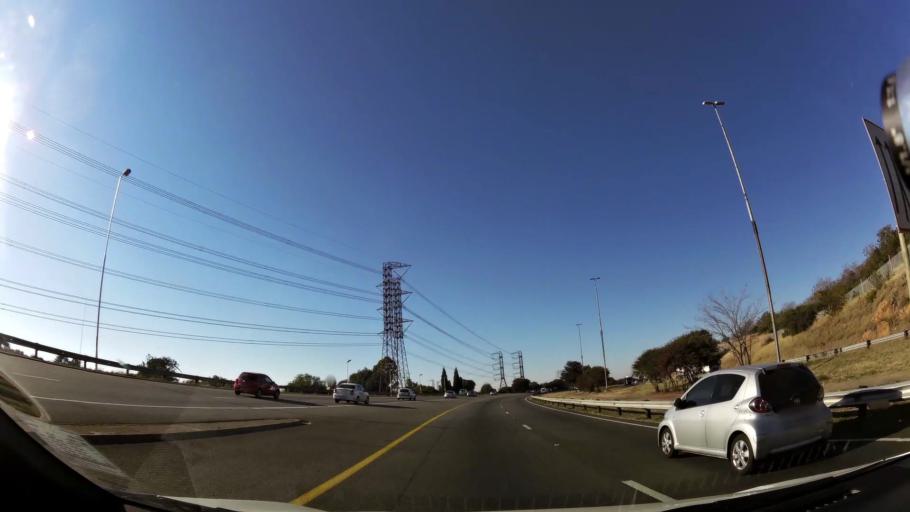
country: ZA
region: Gauteng
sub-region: Ekurhuleni Metropolitan Municipality
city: Germiston
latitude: -26.2691
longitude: 28.1012
